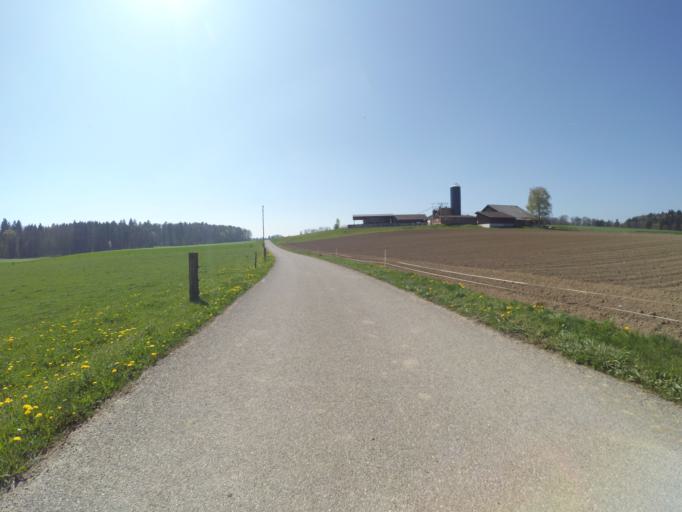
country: CH
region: Thurgau
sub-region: Frauenfeld District
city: Diessenhofen
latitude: 47.6370
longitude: 8.7392
